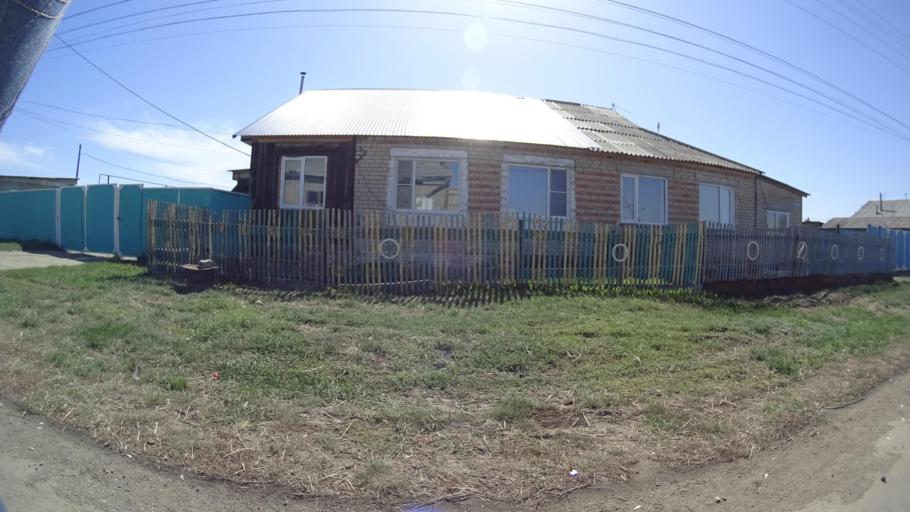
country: RU
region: Chelyabinsk
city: Chesma
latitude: 53.7952
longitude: 61.0342
